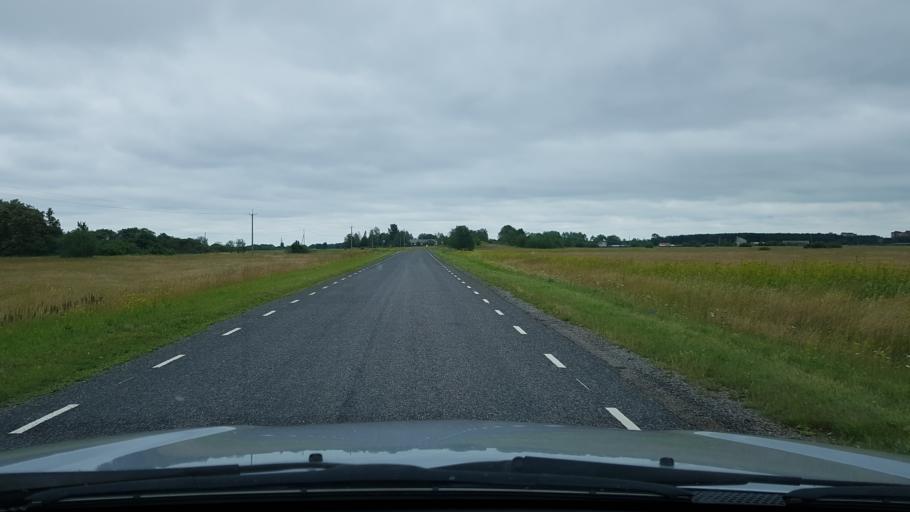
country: EE
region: Ida-Virumaa
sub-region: Narva linn
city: Narva
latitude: 59.3804
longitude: 28.1276
